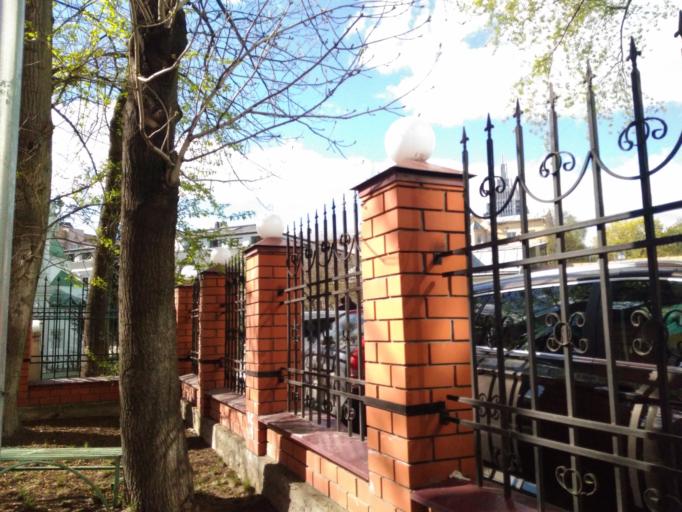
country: RU
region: Moscow
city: Moscow
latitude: 55.7689
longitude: 37.6080
